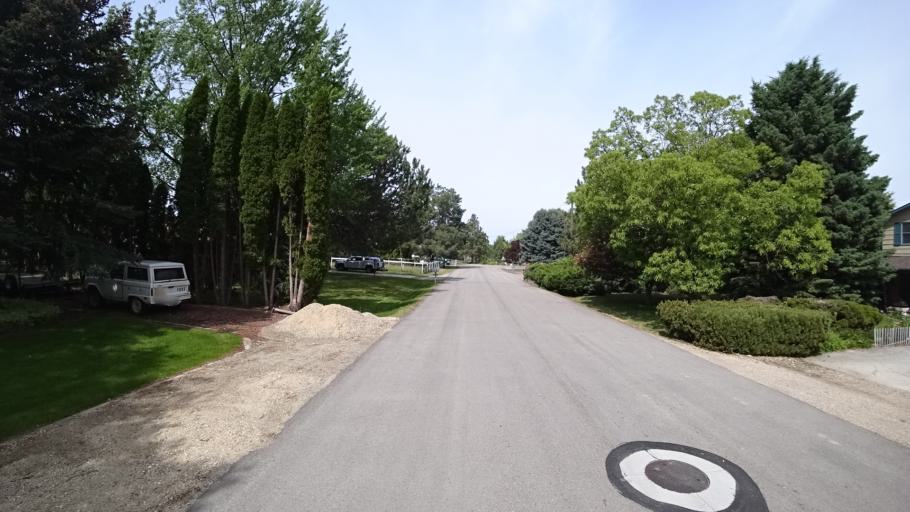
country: US
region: Idaho
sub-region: Ada County
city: Meridian
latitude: 43.5801
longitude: -116.3220
